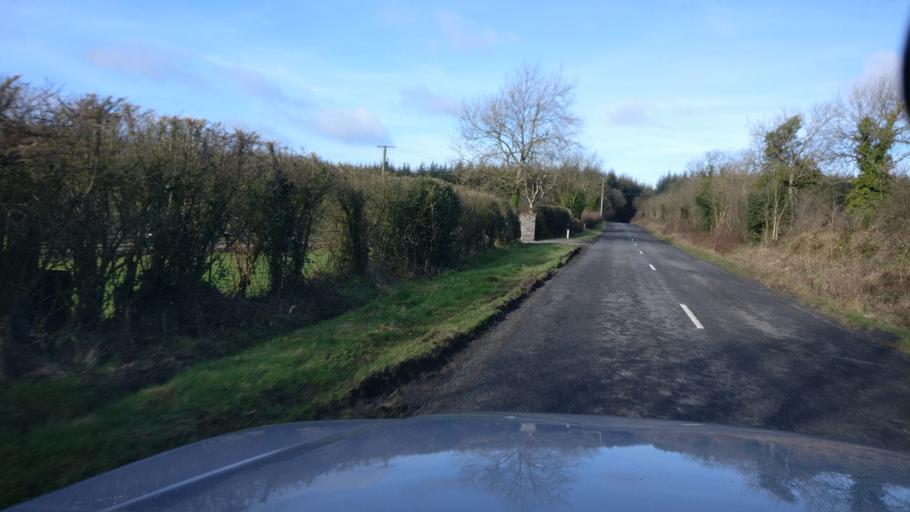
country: IE
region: Leinster
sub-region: Kilkenny
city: Castlecomer
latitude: 52.9090
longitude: -7.1832
